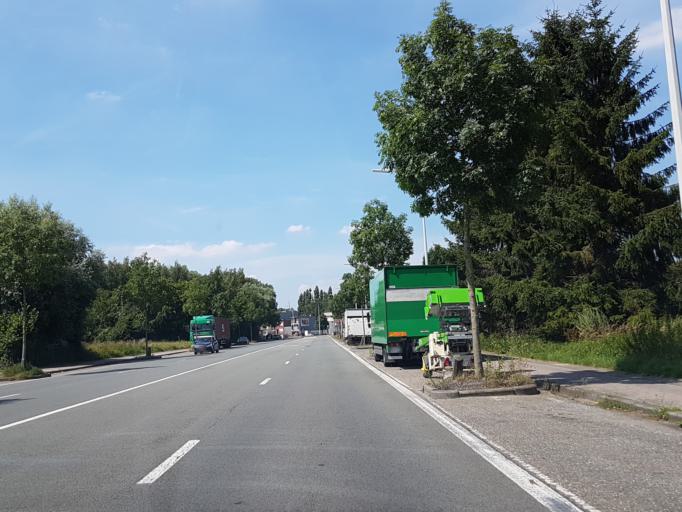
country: BE
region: Flanders
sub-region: Provincie Antwerpen
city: Borsbeek
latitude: 51.2061
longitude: 4.4811
